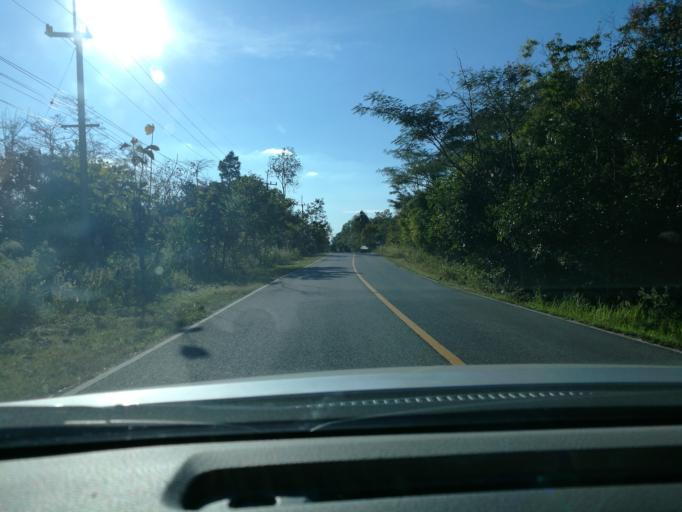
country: TH
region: Phitsanulok
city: Nakhon Thai
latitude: 17.0220
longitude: 100.9794
